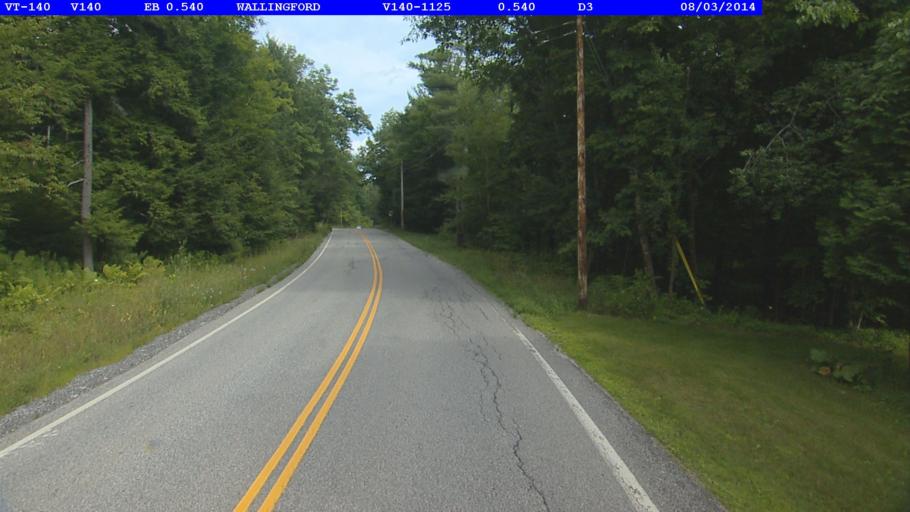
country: US
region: Vermont
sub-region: Rutland County
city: Rutland
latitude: 43.4684
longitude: -72.9679
